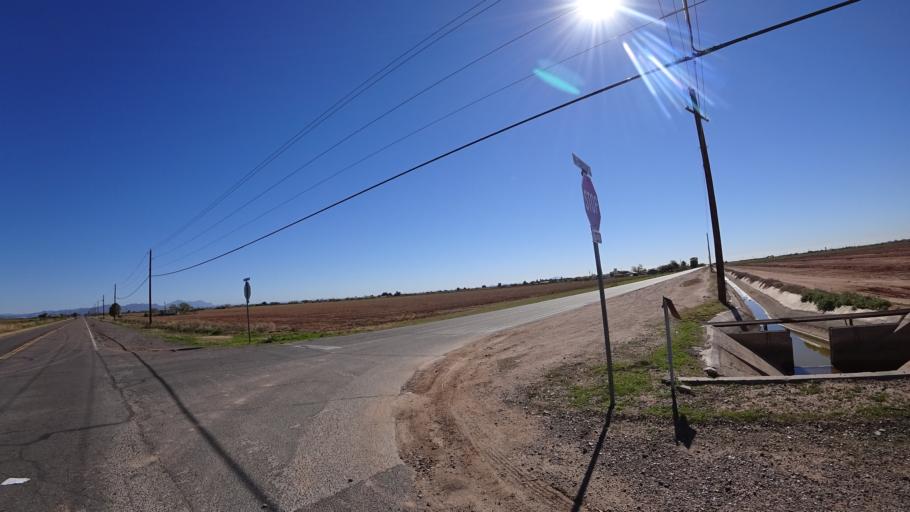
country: US
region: Arizona
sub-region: Maricopa County
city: Scottsdale
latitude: 33.5095
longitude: -111.8742
